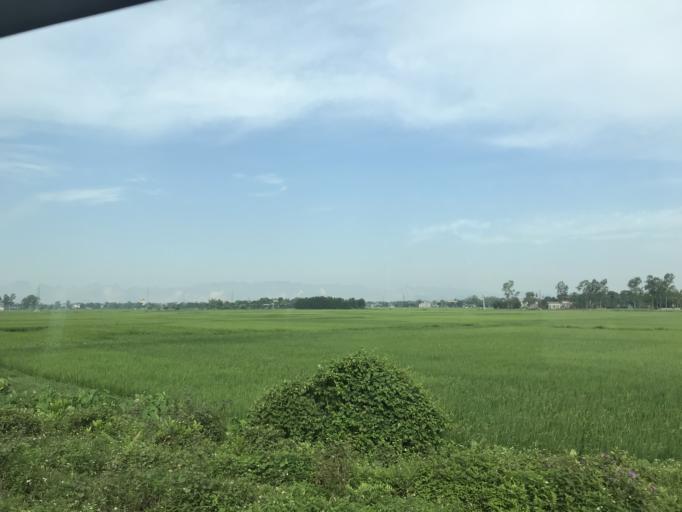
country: VN
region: Ha Nam
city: Thanh Pho Phu Ly
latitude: 20.5175
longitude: 105.9428
